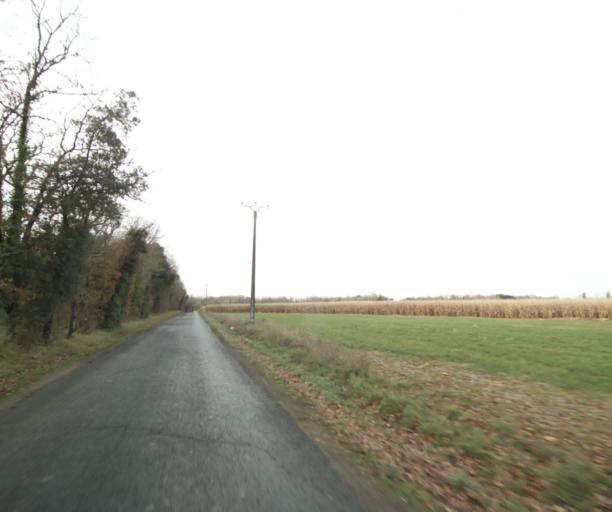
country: FR
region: Poitou-Charentes
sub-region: Departement de la Charente-Maritime
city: Saint-Hilaire-de-Villefranche
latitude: 45.8254
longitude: -0.5760
